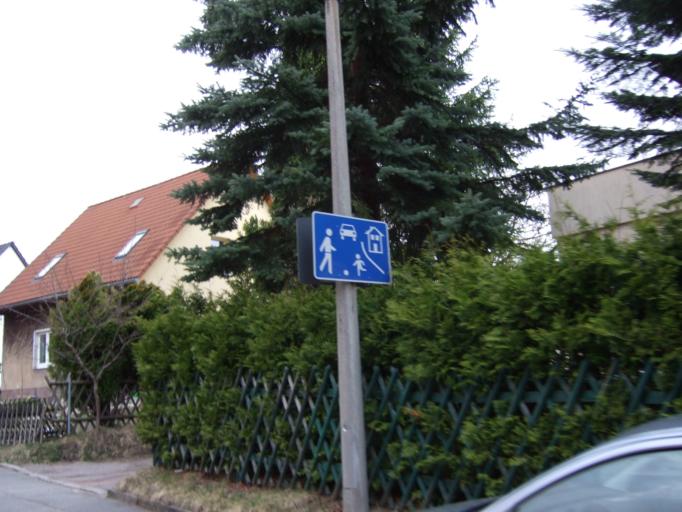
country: DE
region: Saxony
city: Freiberg
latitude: 50.9158
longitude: 13.3308
